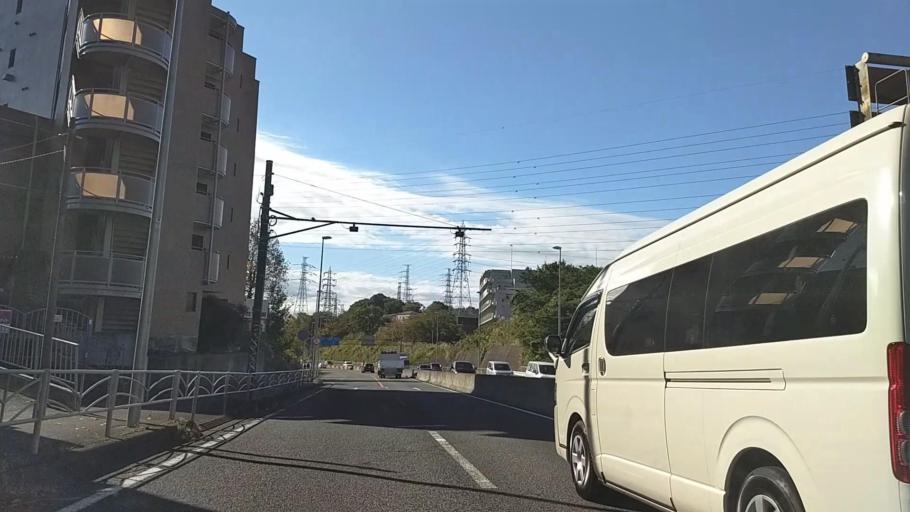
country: JP
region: Kanagawa
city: Fujisawa
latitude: 35.4041
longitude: 139.5277
